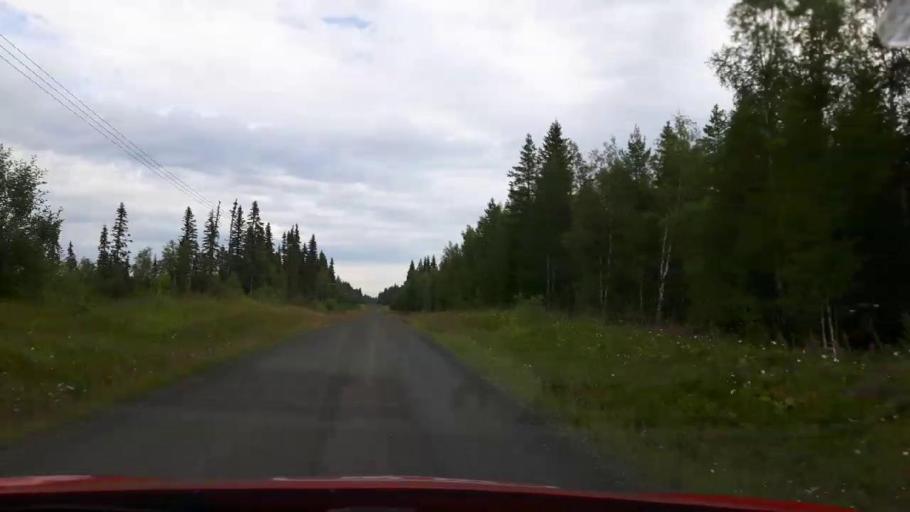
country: SE
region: Jaemtland
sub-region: Stroemsunds Kommun
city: Stroemsund
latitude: 63.5049
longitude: 15.3345
